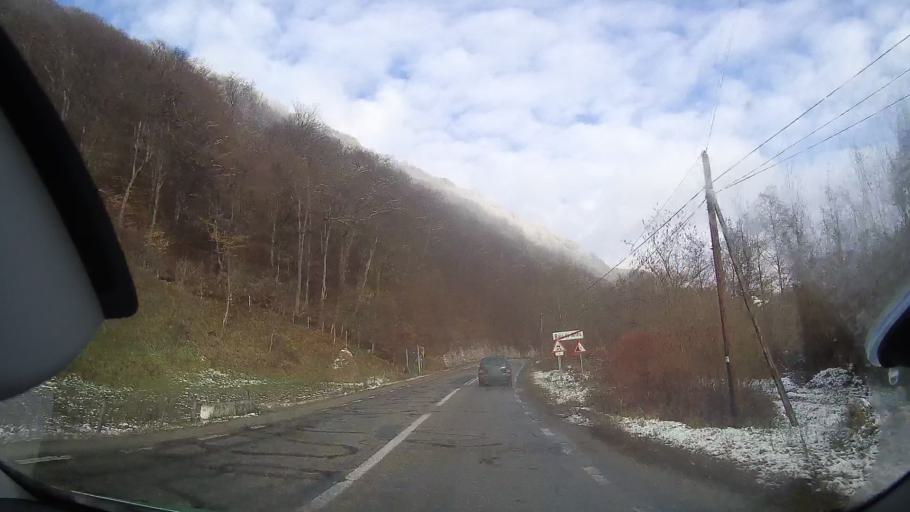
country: RO
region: Alba
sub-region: Oras Baia de Aries
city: Baia de Aries
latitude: 46.3874
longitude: 23.2800
